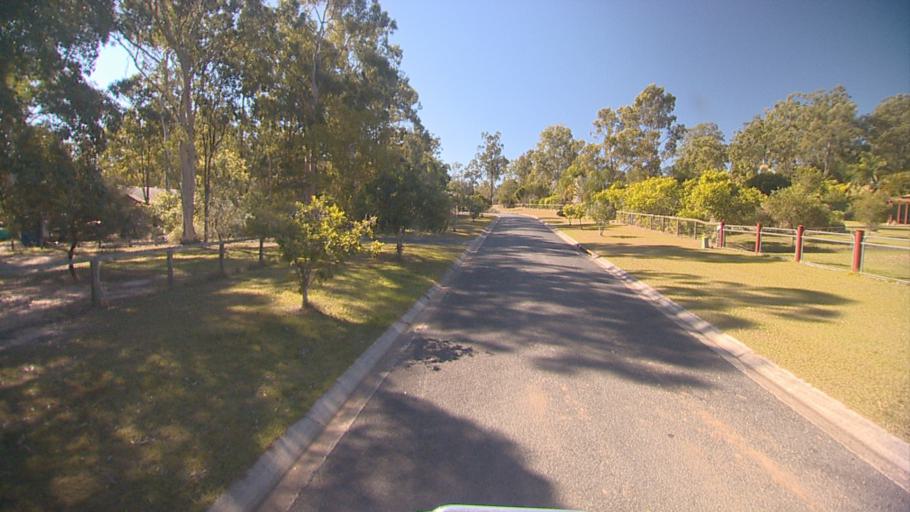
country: AU
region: Queensland
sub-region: Logan
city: North Maclean
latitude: -27.8255
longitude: 152.9408
